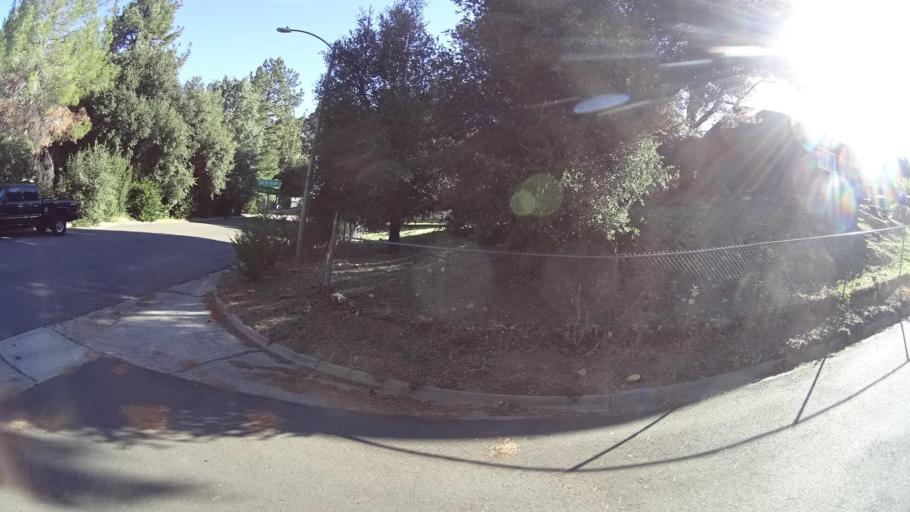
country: US
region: California
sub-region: San Diego County
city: Pine Valley
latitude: 32.8266
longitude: -116.5224
